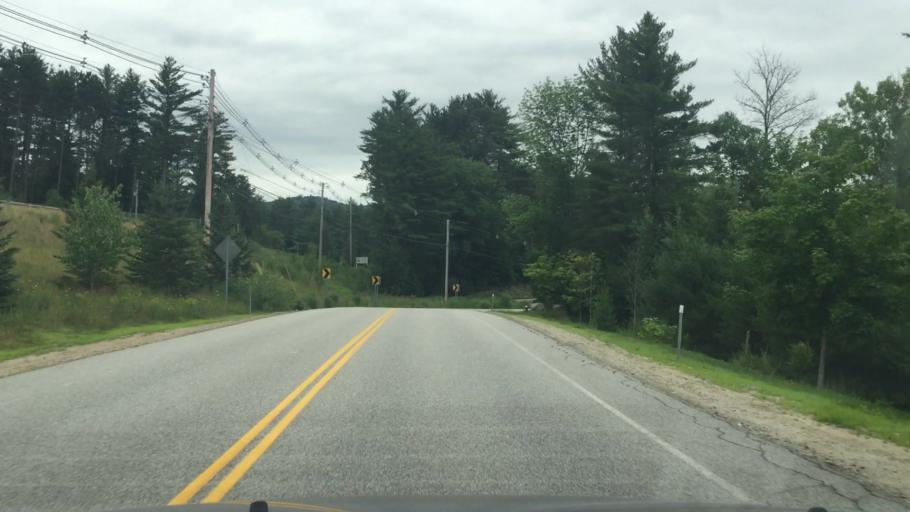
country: US
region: New Hampshire
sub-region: Carroll County
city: North Conway
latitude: 44.0896
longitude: -71.2046
